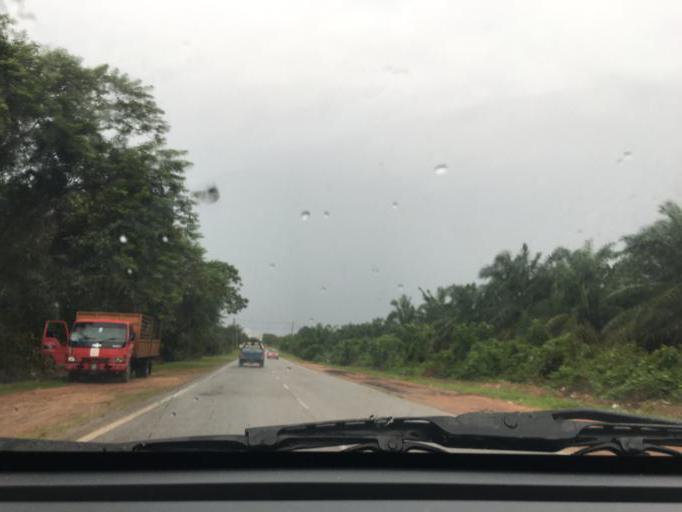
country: MY
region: Kedah
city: Sungai Petani
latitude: 5.6166
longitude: 100.6390
